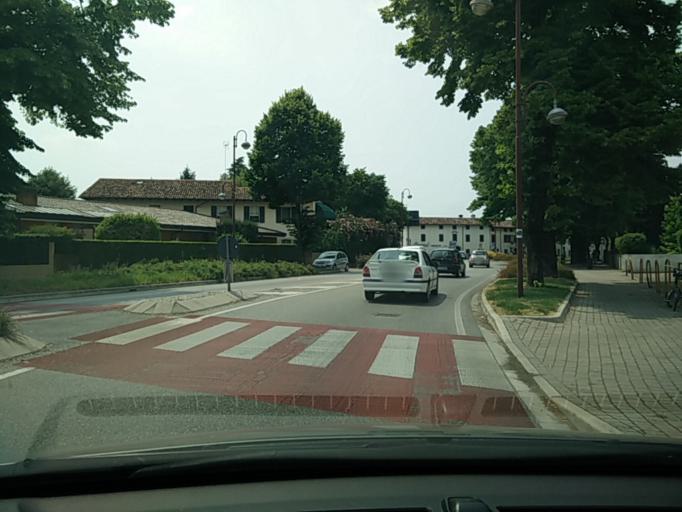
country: IT
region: Friuli Venezia Giulia
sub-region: Provincia di Pordenone
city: San Vito al Tagliamento
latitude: 45.9174
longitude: 12.8646
